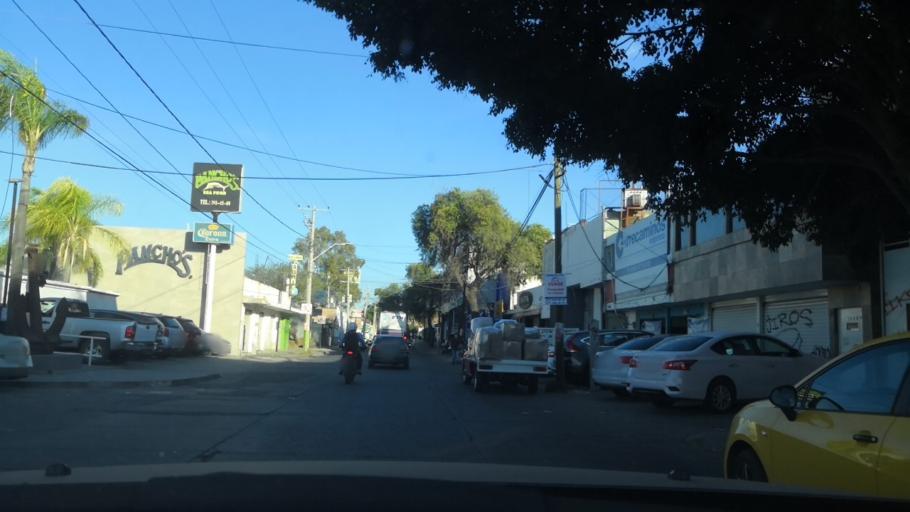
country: MX
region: Guanajuato
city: Leon
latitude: 21.1217
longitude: -101.6595
